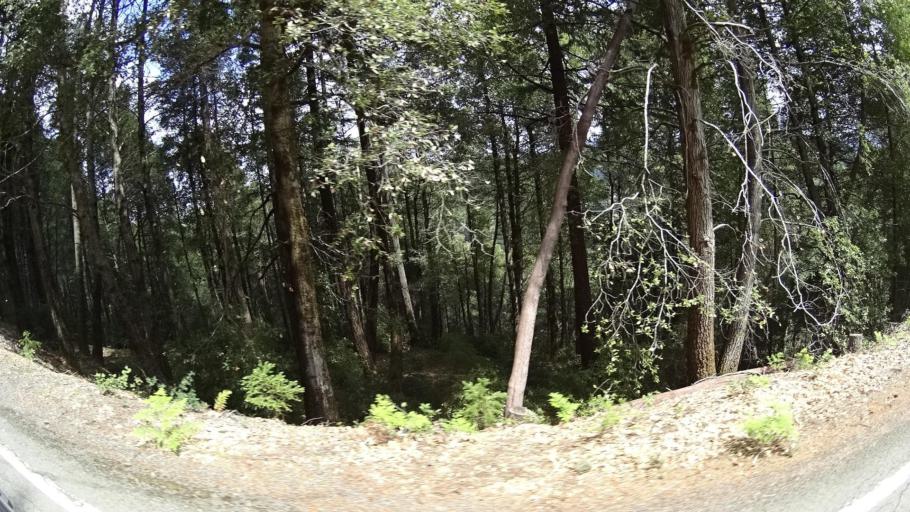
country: US
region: California
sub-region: Humboldt County
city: Redway
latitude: 40.0554
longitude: -123.9915
